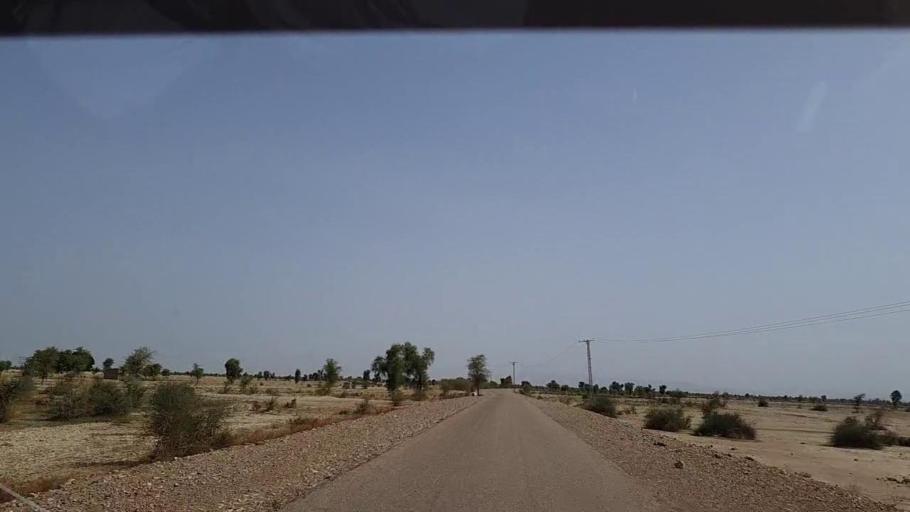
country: PK
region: Sindh
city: Johi
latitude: 26.6598
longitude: 67.5060
